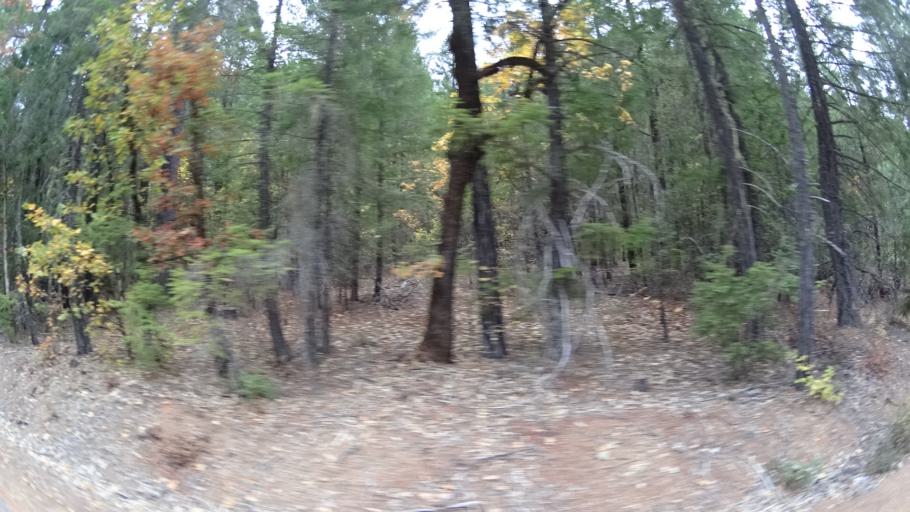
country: US
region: California
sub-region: Siskiyou County
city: Happy Camp
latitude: 41.8797
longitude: -123.4361
